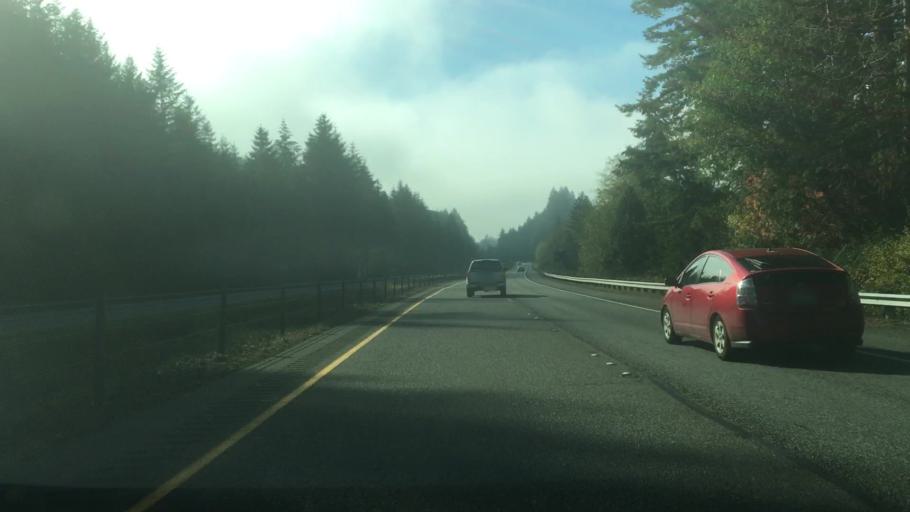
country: US
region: Washington
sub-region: Grays Harbor County
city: McCleary
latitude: 47.0409
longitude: -123.3225
